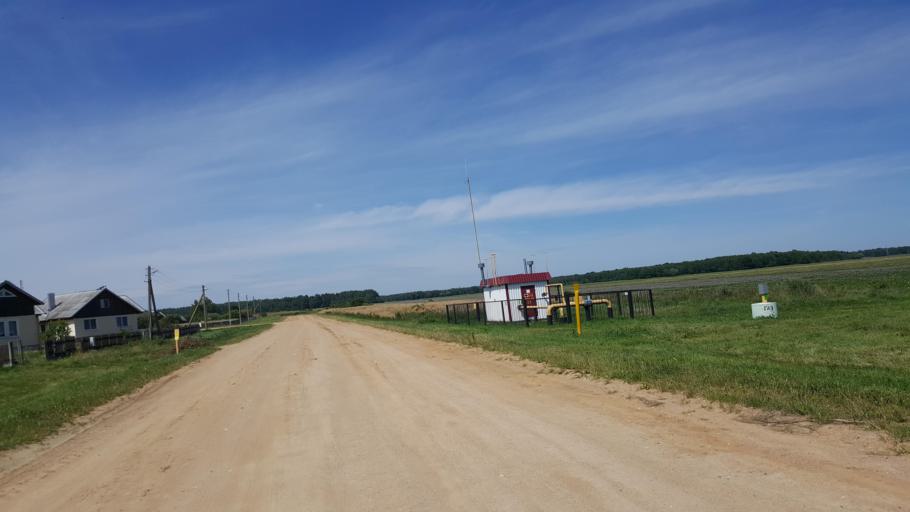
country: BY
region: Brest
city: Pruzhany
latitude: 52.5636
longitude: 24.2277
